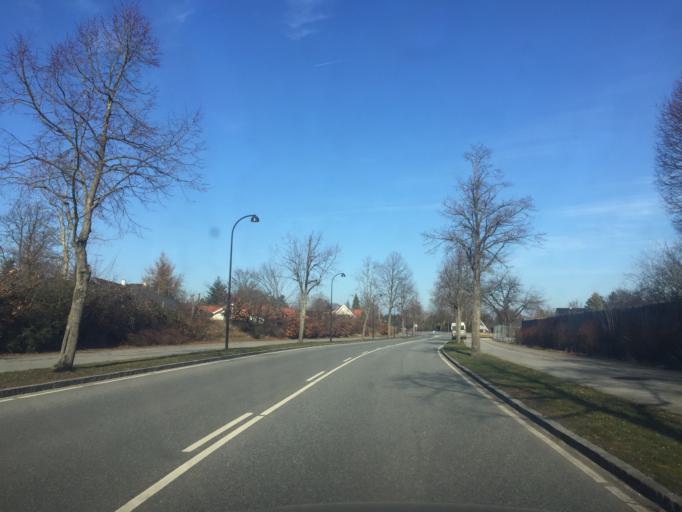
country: DK
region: Capital Region
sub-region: Rudersdal Kommune
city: Trorod
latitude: 55.8437
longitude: 12.5317
